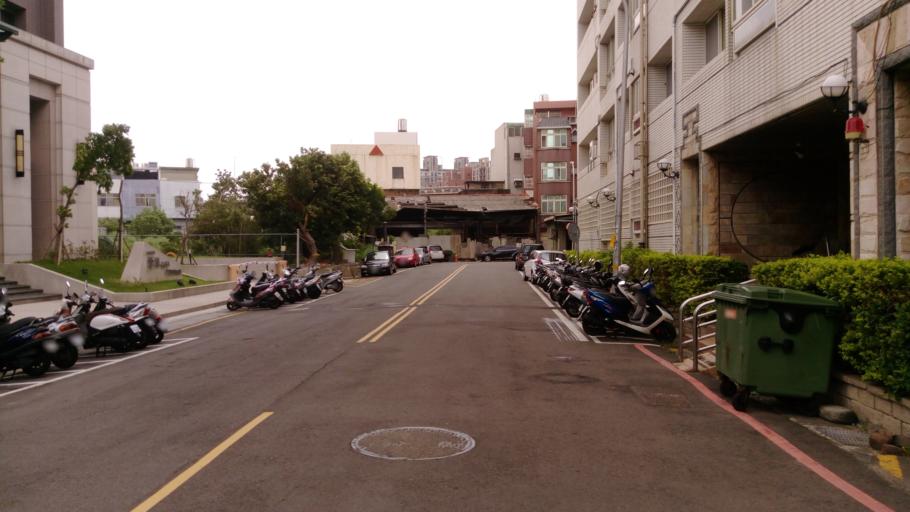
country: TW
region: Taiwan
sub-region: Hsinchu
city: Hsinchu
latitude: 24.7942
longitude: 120.9499
